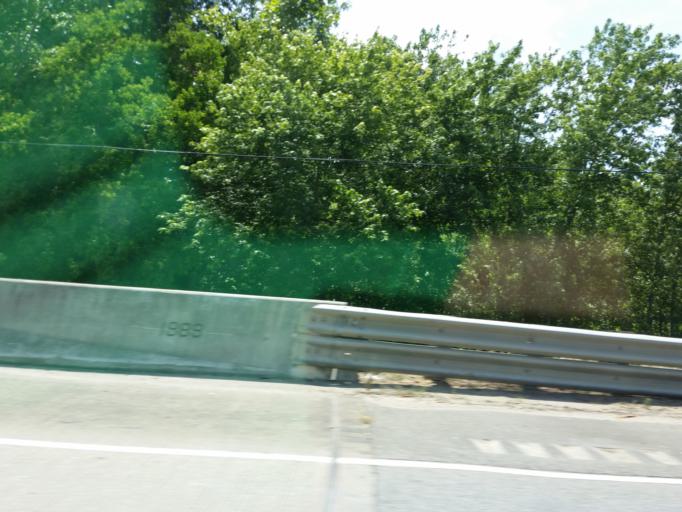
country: US
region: Alabama
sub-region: Marengo County
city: Demopolis
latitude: 32.5265
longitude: -87.8375
